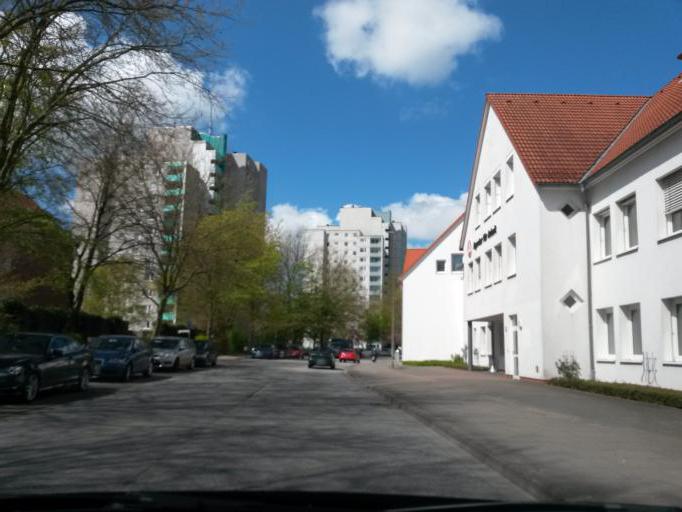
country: DE
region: Schleswig-Holstein
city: Uetersen
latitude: 53.6814
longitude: 9.6659
